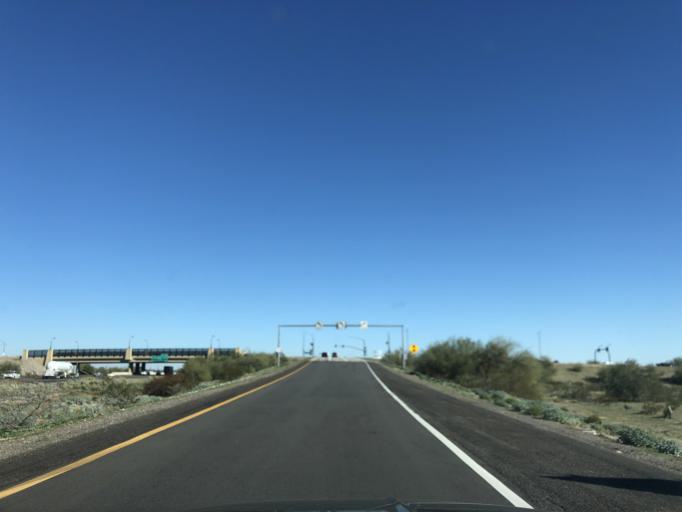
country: US
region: Arizona
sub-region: Maricopa County
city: Citrus Park
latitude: 33.4602
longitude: -112.5071
